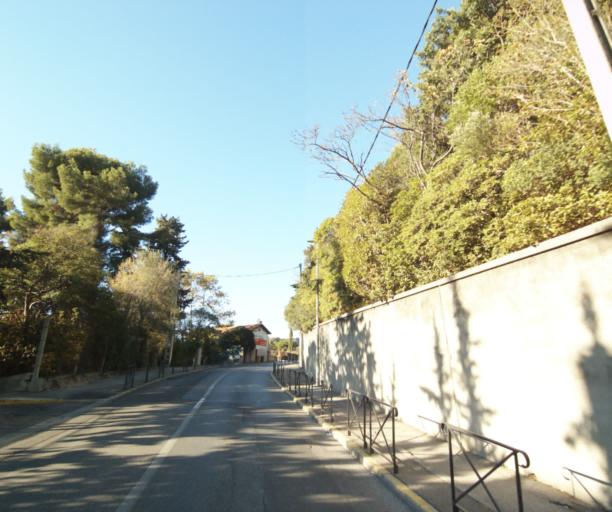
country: FR
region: Provence-Alpes-Cote d'Azur
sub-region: Departement des Bouches-du-Rhone
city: Cassis
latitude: 43.2157
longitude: 5.5433
